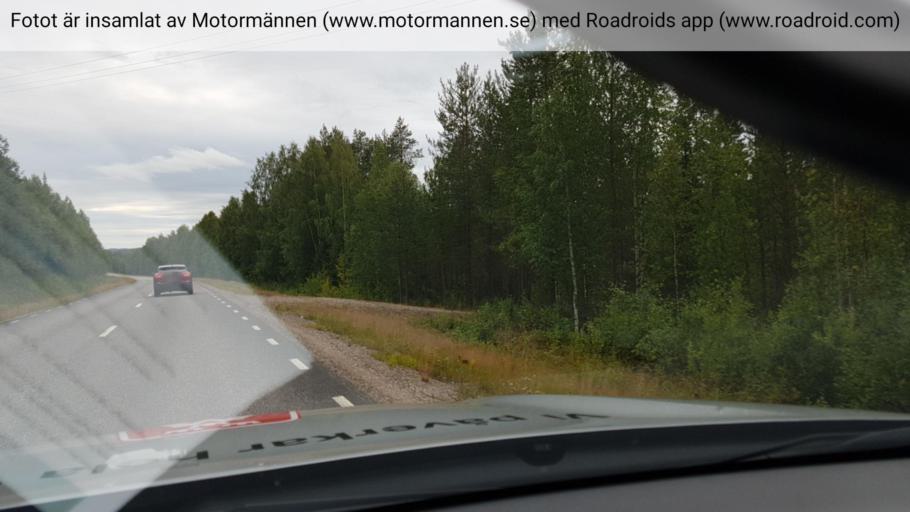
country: SE
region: Norrbotten
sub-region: Overkalix Kommun
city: OEverkalix
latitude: 66.5465
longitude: 22.7552
